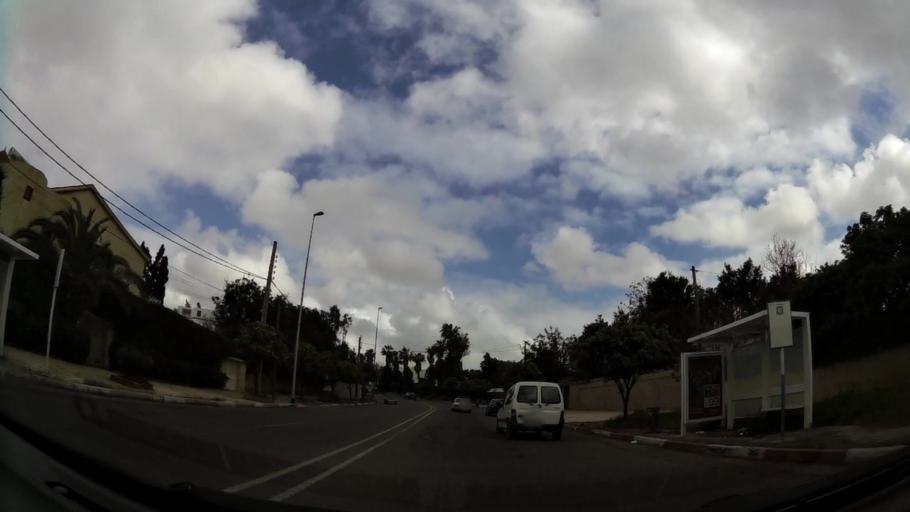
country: MA
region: Grand Casablanca
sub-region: Casablanca
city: Casablanca
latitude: 33.5497
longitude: -7.6202
